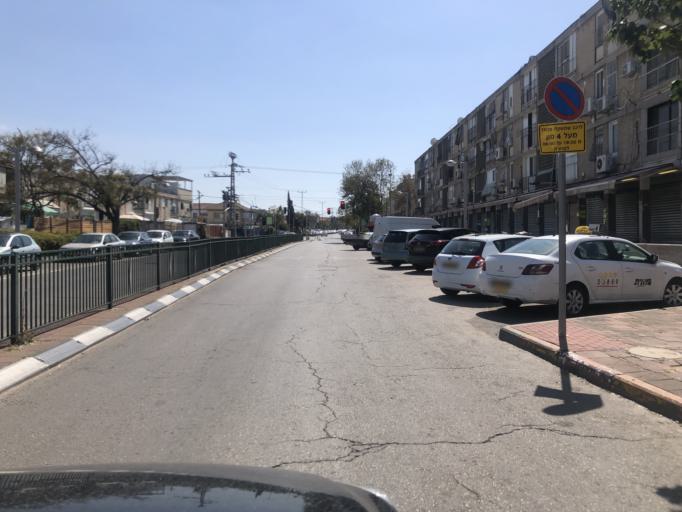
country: IL
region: Tel Aviv
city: Holon
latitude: 32.0113
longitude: 34.7648
